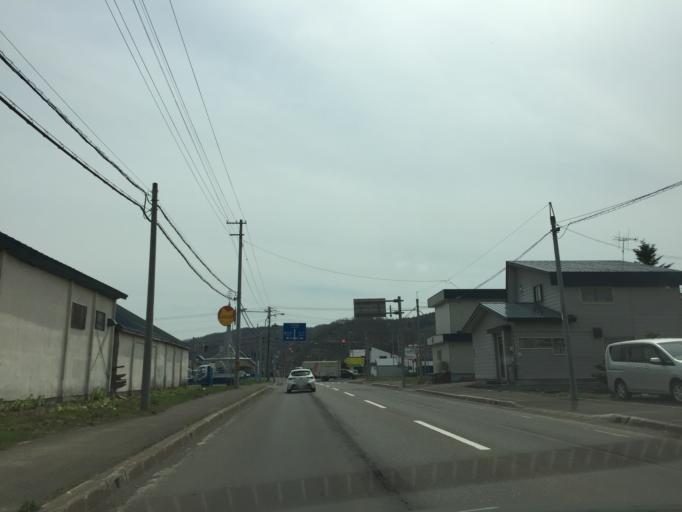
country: JP
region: Hokkaido
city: Ashibetsu
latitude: 43.5318
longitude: 142.1705
